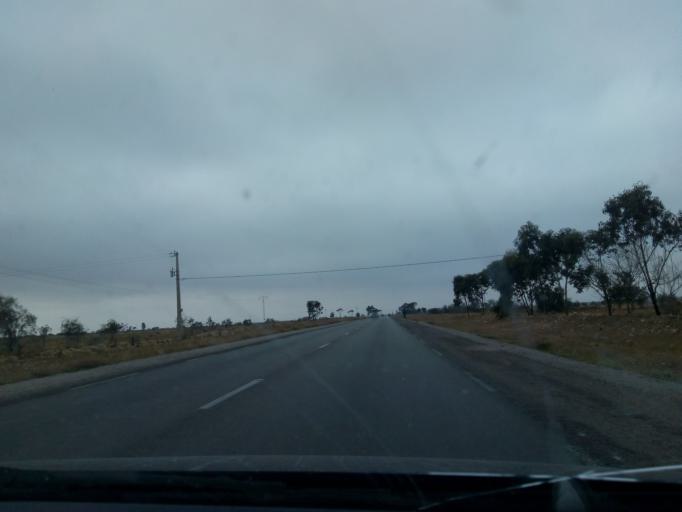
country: TN
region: Madanin
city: Medenine
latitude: 33.2770
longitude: 10.4689
